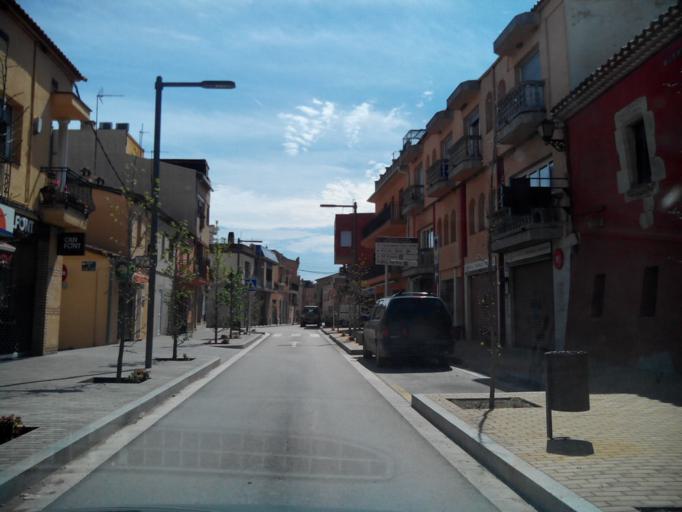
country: ES
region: Catalonia
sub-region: Provincia de Girona
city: Sant Pere Pescador
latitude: 42.1883
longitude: 3.0826
